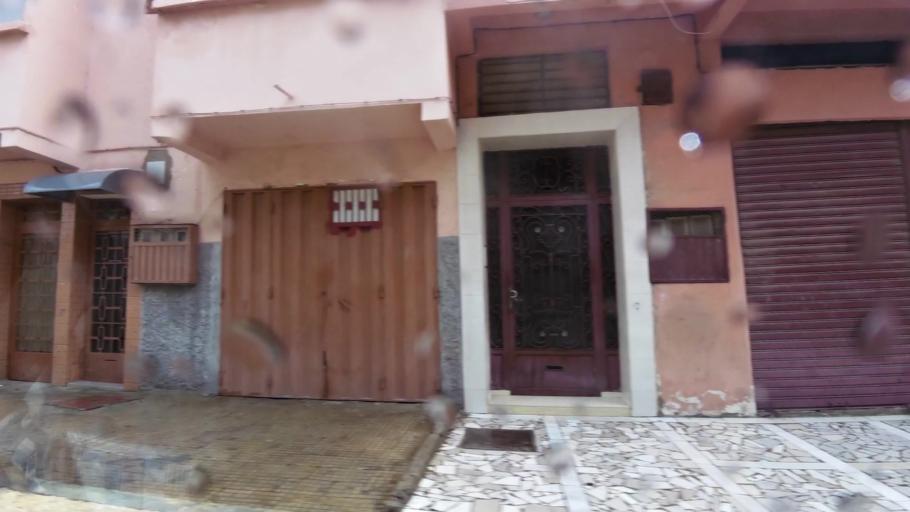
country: MA
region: Grand Casablanca
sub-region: Casablanca
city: Casablanca
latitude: 33.5521
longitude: -7.6747
